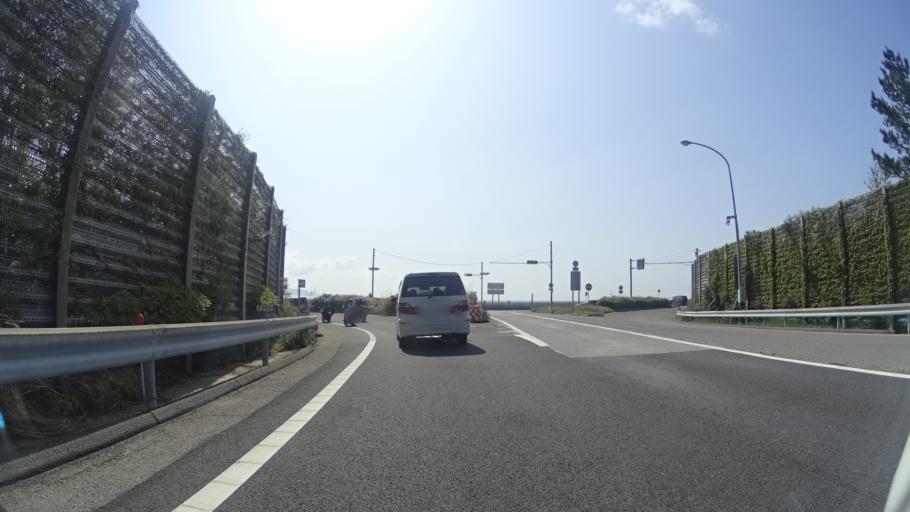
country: JP
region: Tokushima
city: Narutocho-mitsuishi
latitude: 34.2176
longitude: 134.6299
